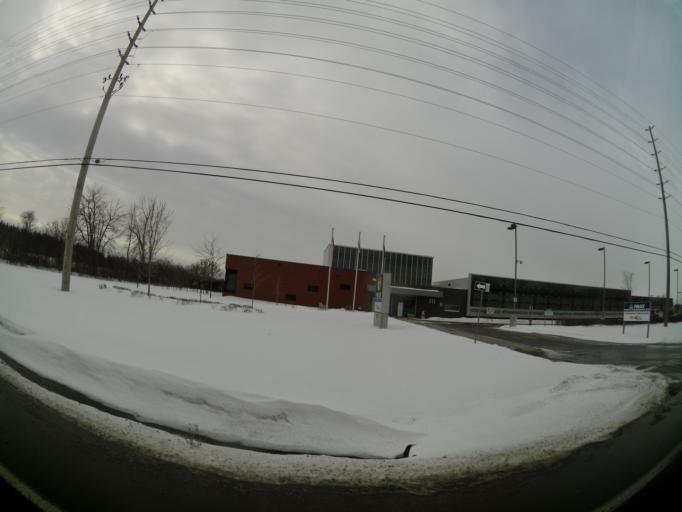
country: CA
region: Ontario
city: Bells Corners
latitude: 45.2933
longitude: -75.9260
